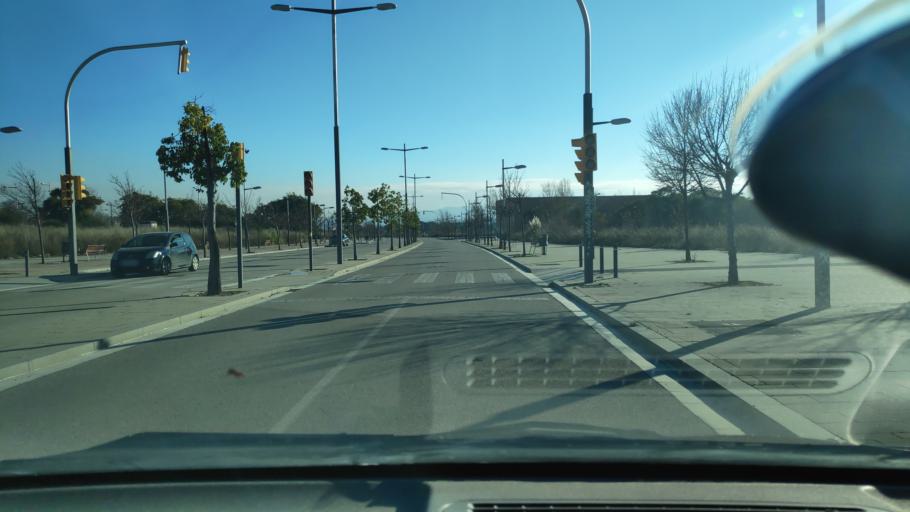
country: ES
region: Catalonia
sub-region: Provincia de Barcelona
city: Sant Quirze del Valles
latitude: 41.5465
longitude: 2.0794
